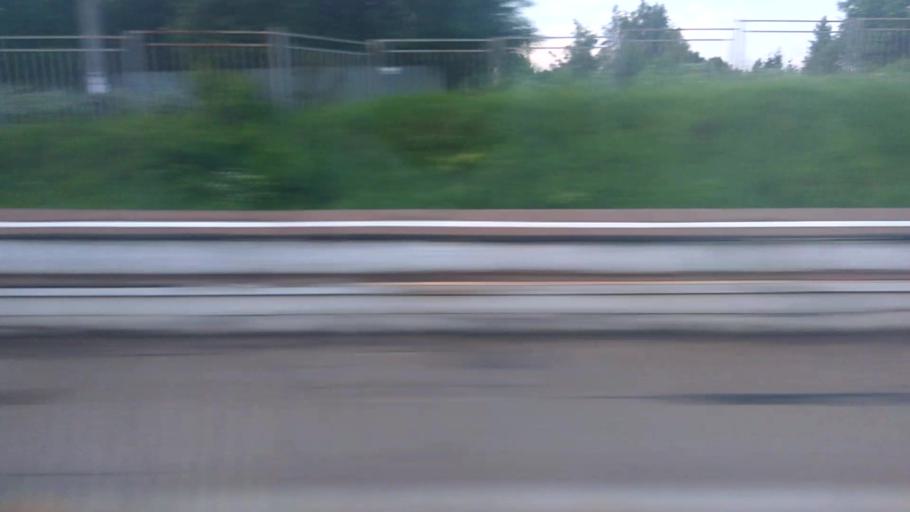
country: RU
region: Moskovskaya
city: Vostryakovo
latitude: 55.3831
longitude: 37.8142
